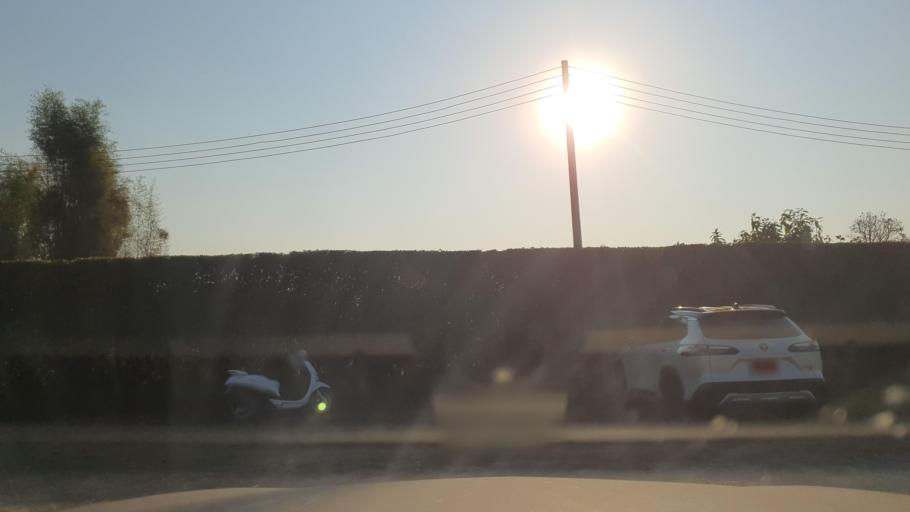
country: TH
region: Chiang Rai
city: Mae Lao
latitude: 19.8530
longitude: 99.7418
